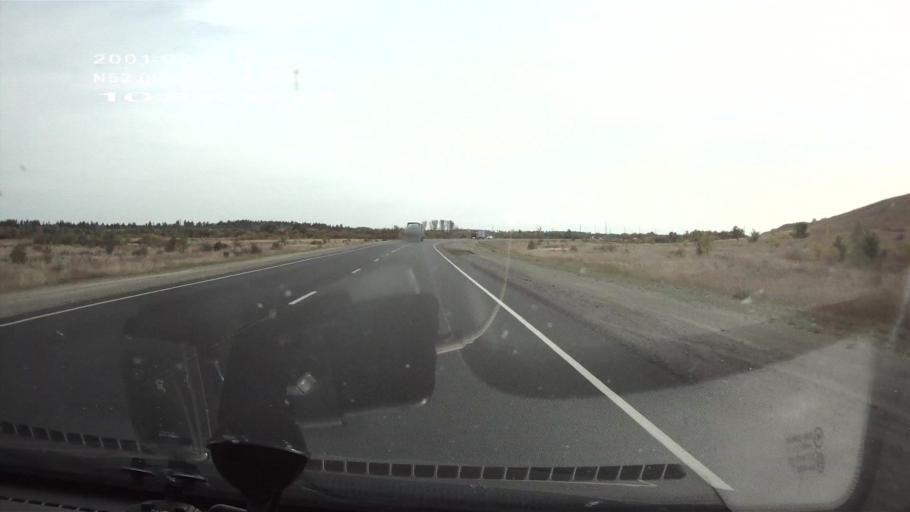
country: RU
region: Saratov
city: Sennoy
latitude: 52.0948
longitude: 46.8132
